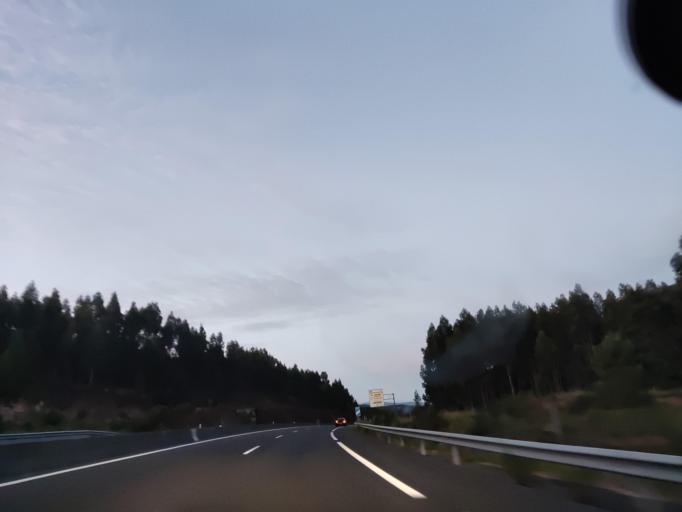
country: ES
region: Galicia
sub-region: Provincia da Coruna
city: Boiro
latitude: 42.6045
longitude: -8.9695
